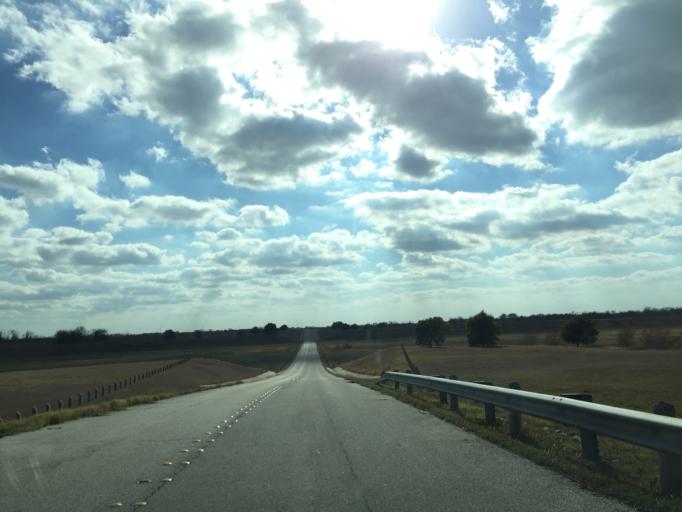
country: US
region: Texas
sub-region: Williamson County
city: Granger
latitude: 30.6844
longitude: -97.3383
